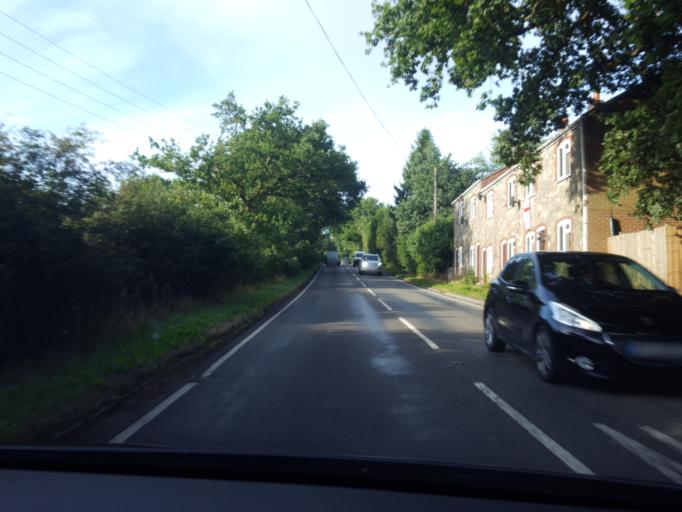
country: GB
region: England
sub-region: Leicestershire
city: Markfield
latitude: 52.7183
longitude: -1.2827
